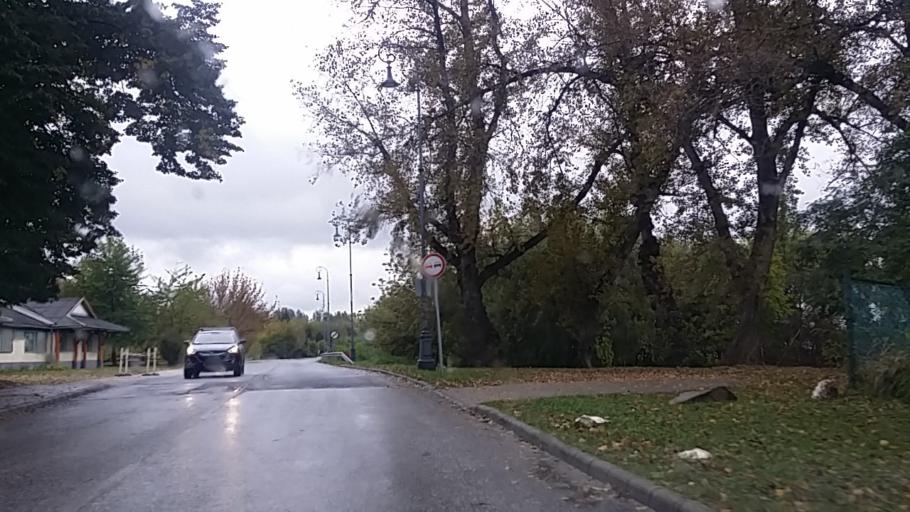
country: HU
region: Komarom-Esztergom
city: Esztergom
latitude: 47.7926
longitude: 18.7324
